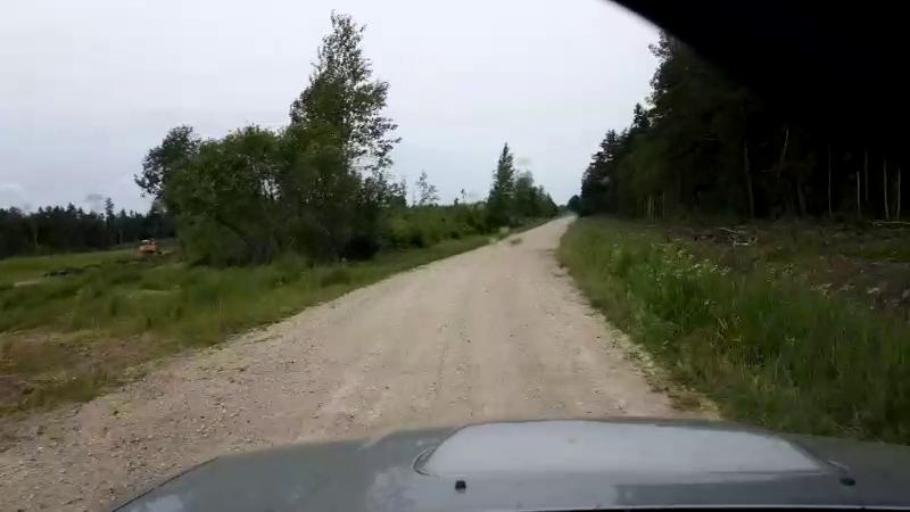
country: EE
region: Paernumaa
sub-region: Halinga vald
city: Parnu-Jaagupi
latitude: 58.5396
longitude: 24.5965
